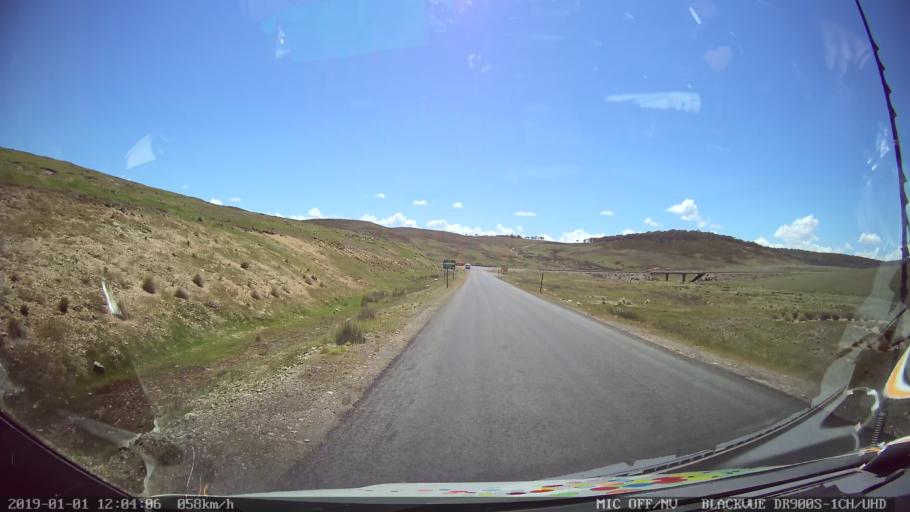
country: AU
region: New South Wales
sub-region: Snowy River
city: Jindabyne
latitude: -35.8683
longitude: 148.4934
